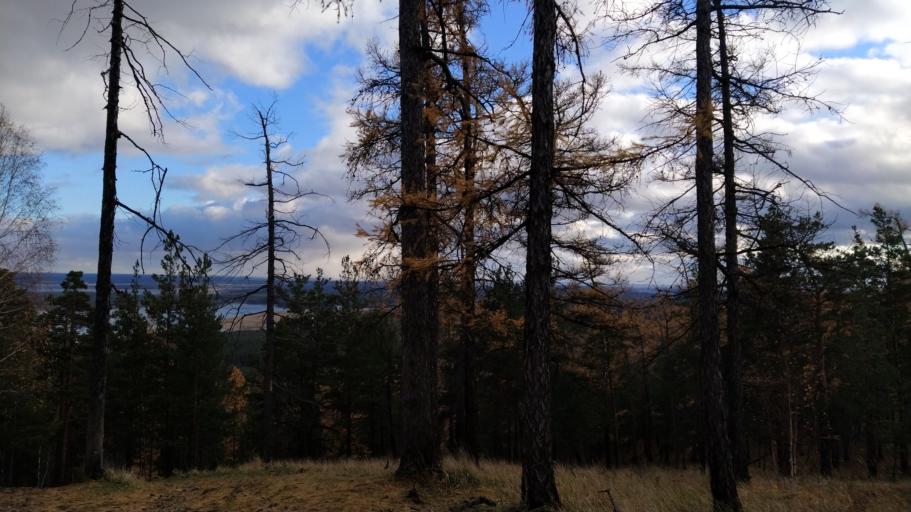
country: RU
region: Chelyabinsk
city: Kyshtym
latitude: 55.7222
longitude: 60.4499
